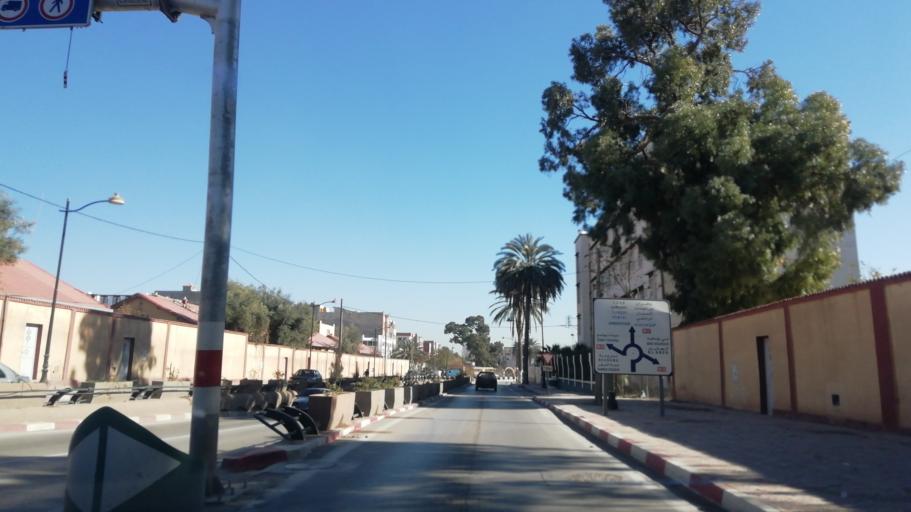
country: DZ
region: Tlemcen
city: Nedroma
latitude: 34.8470
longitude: -1.7313
